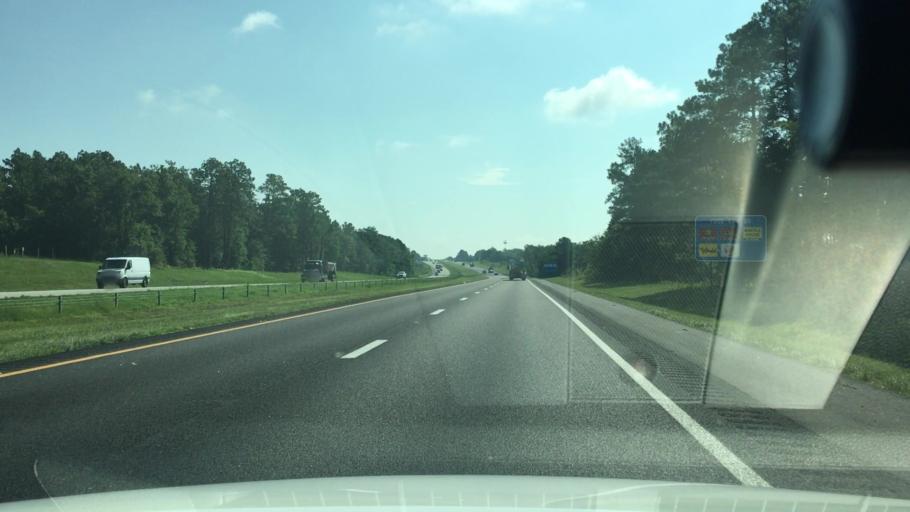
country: US
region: South Carolina
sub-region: Aiken County
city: Aiken
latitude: 33.6593
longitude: -81.6899
